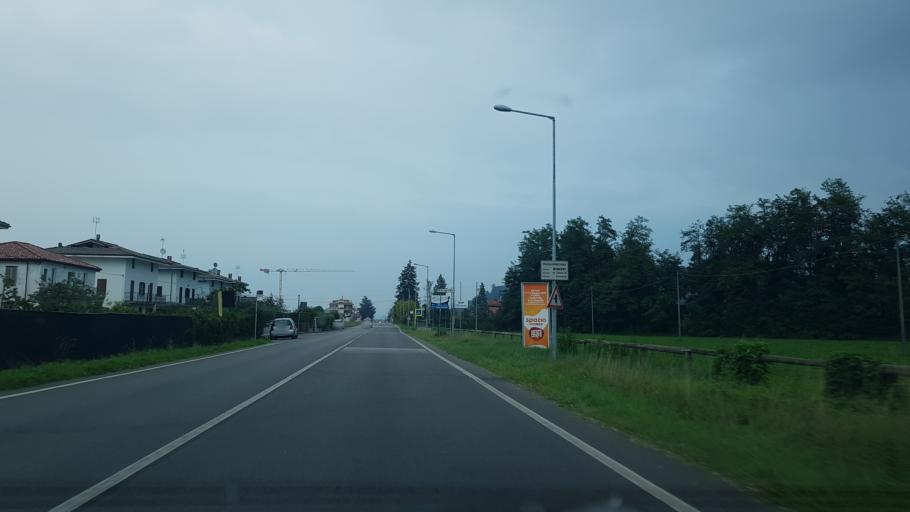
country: IT
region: Piedmont
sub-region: Provincia di Cuneo
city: Mondovi
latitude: 44.3777
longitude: 7.8097
